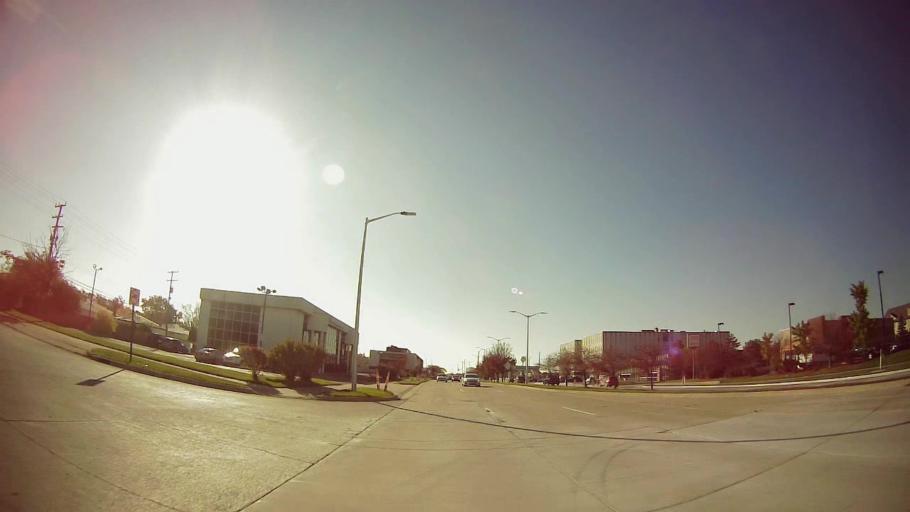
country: US
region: Michigan
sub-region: Oakland County
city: Oak Park
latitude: 42.4620
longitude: -83.2011
